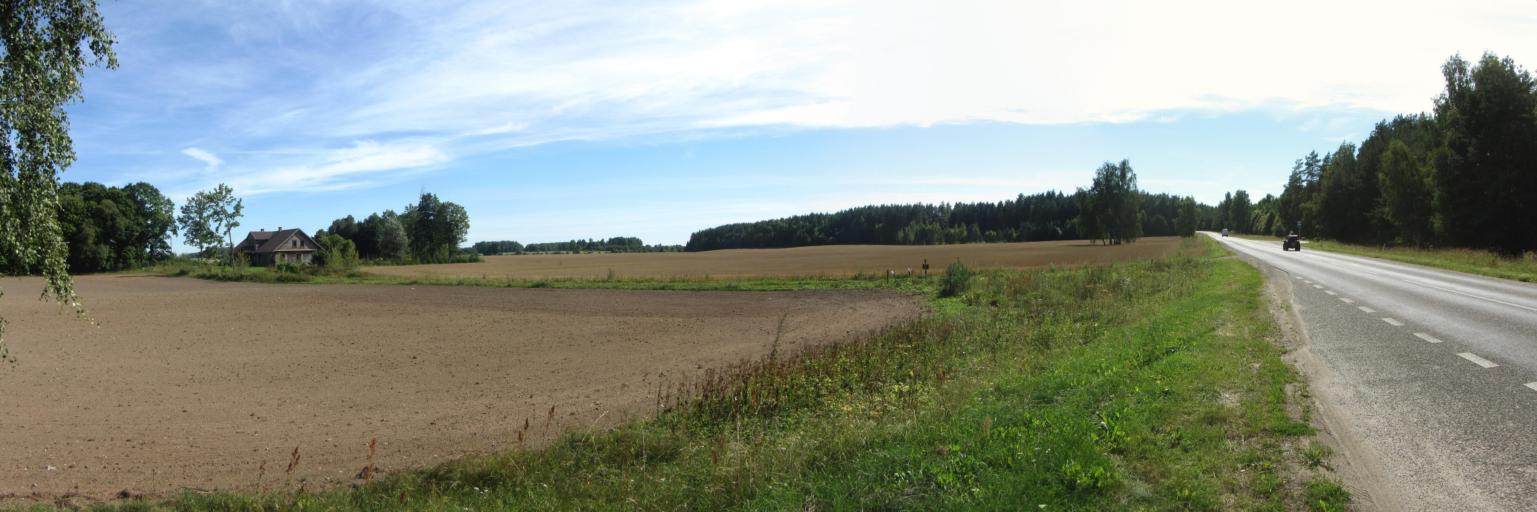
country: LT
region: Utenos apskritis
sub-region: Utena
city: Utena
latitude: 55.7136
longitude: 25.4121
